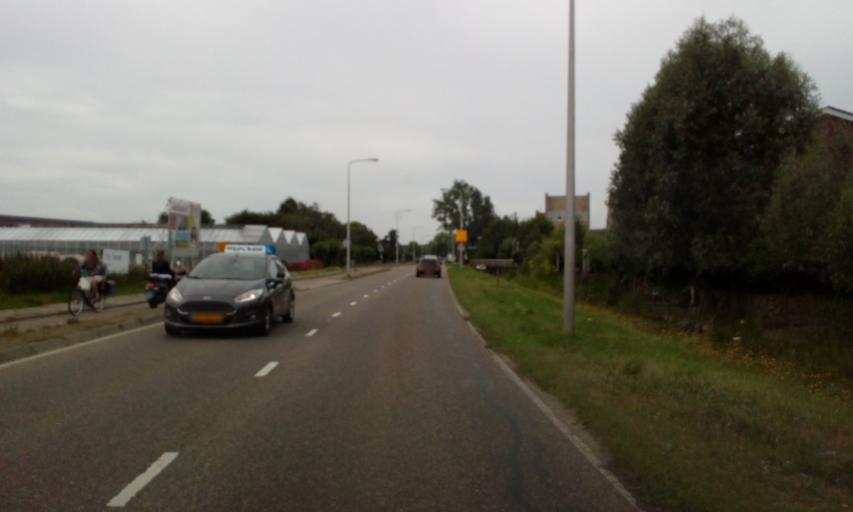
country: NL
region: South Holland
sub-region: Gemeente Westland
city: Kwintsheul
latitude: 52.0322
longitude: 4.2776
